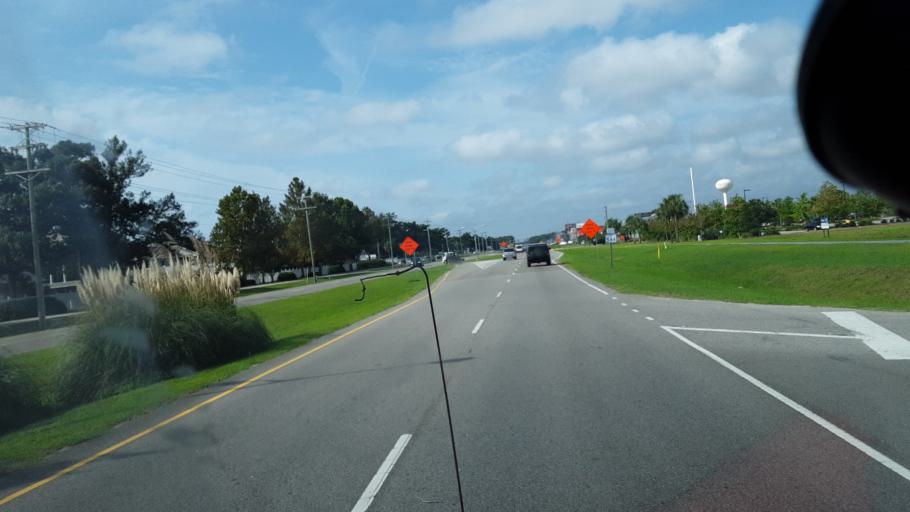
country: US
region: South Carolina
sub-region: Horry County
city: Surfside Beach
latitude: 33.6326
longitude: -78.9588
